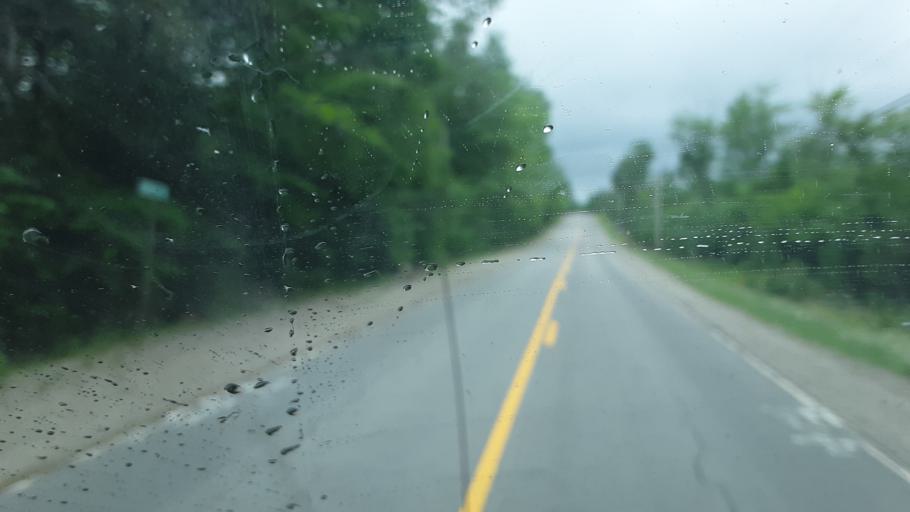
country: US
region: Maine
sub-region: Penobscot County
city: Millinocket
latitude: 45.6911
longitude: -68.7868
